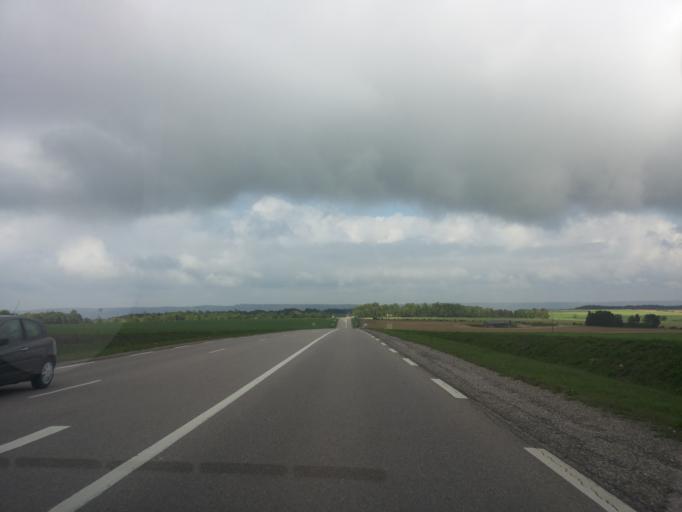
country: FR
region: Lorraine
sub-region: Departement des Vosges
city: Neufchateau
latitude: 48.3483
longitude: 5.7357
